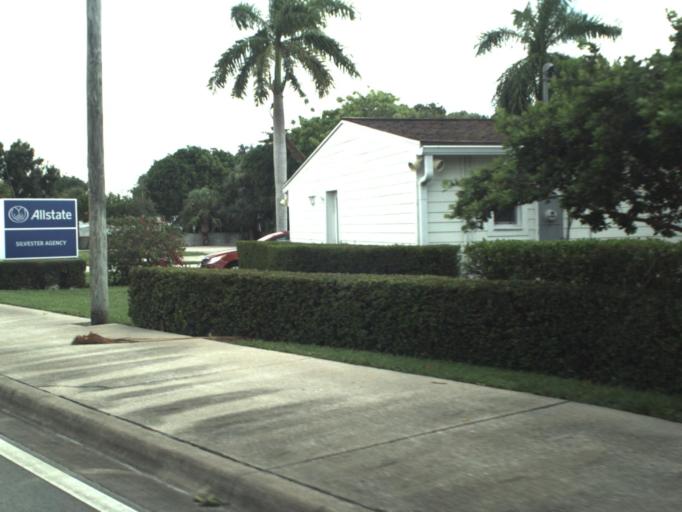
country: US
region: Florida
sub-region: Palm Beach County
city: North Palm Beach
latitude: 26.8110
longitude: -80.0771
